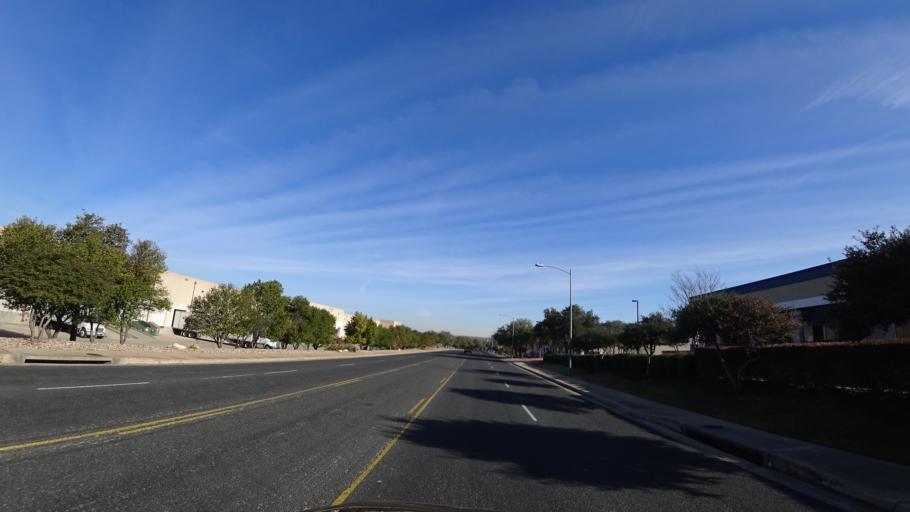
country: US
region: Texas
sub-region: Travis County
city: Wells Branch
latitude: 30.3982
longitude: -97.7098
